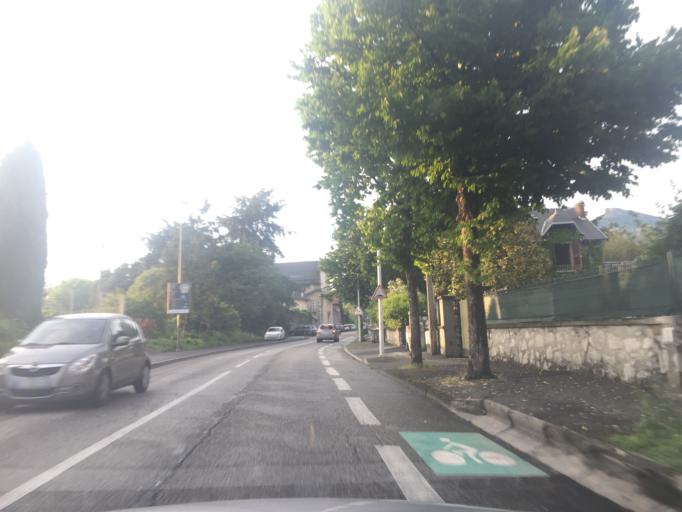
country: FR
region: Rhone-Alpes
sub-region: Departement de la Savoie
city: Chambery
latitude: 45.5697
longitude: 5.9224
